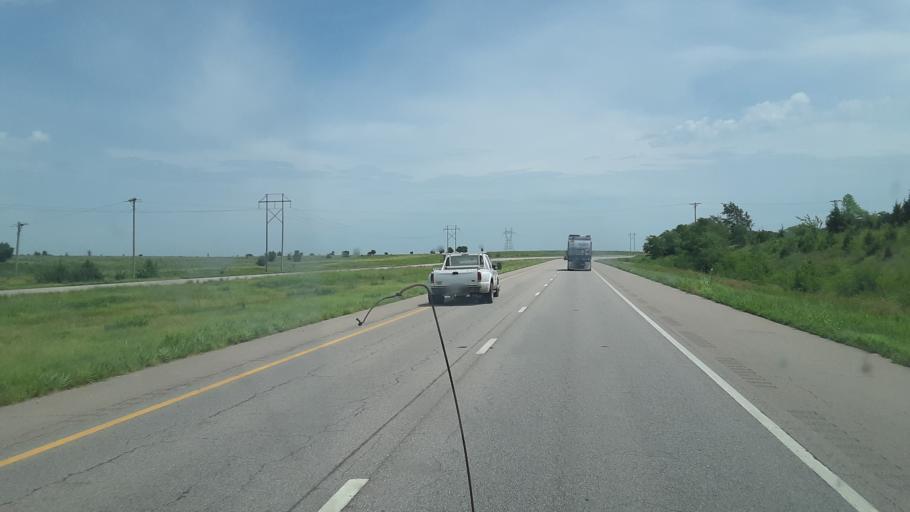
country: US
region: Kansas
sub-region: Butler County
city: Towanda
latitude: 37.8019
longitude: -97.0033
